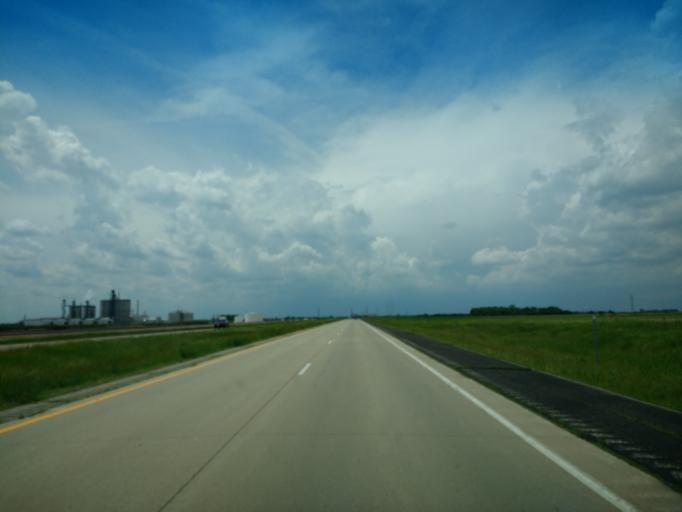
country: US
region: Minnesota
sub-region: Cottonwood County
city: Windom
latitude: 43.8122
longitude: -95.2786
